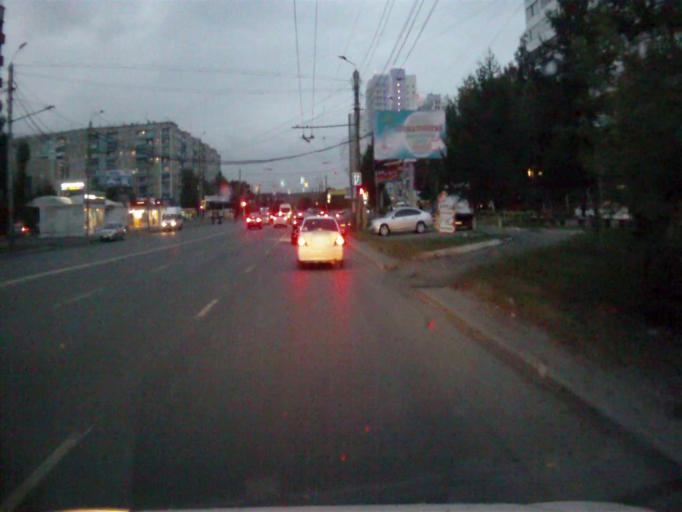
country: RU
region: Chelyabinsk
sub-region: Gorod Chelyabinsk
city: Chelyabinsk
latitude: 55.1800
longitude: 61.3326
